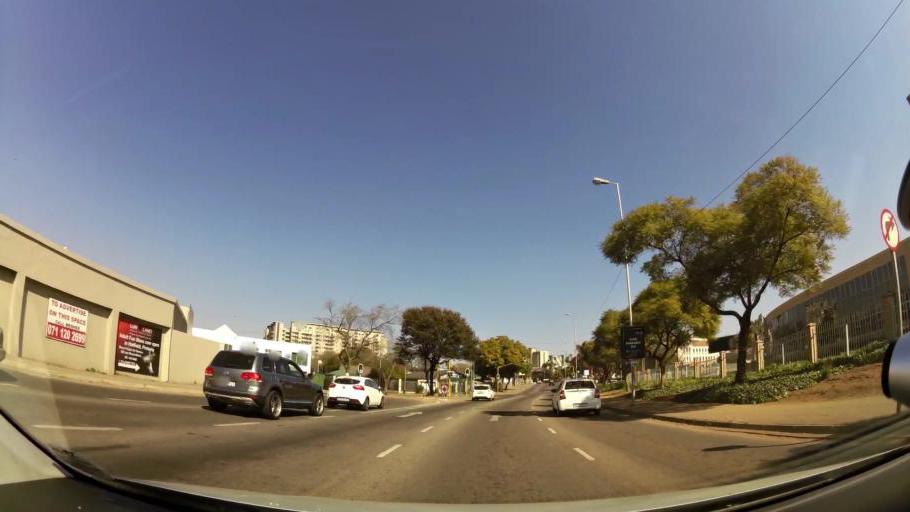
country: ZA
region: Gauteng
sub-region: City of Tshwane Metropolitan Municipality
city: Pretoria
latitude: -25.7453
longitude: 28.2418
